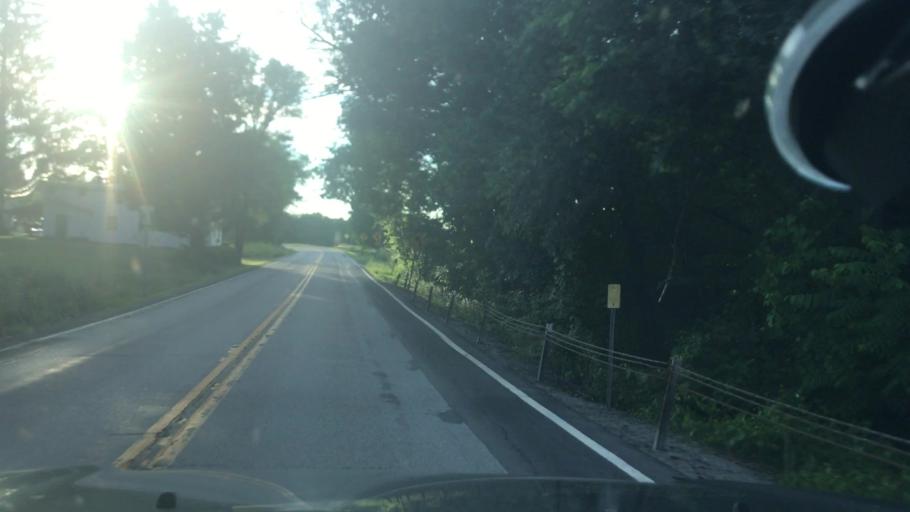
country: US
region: New York
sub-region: Otsego County
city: Unadilla
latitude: 42.3371
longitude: -75.2417
